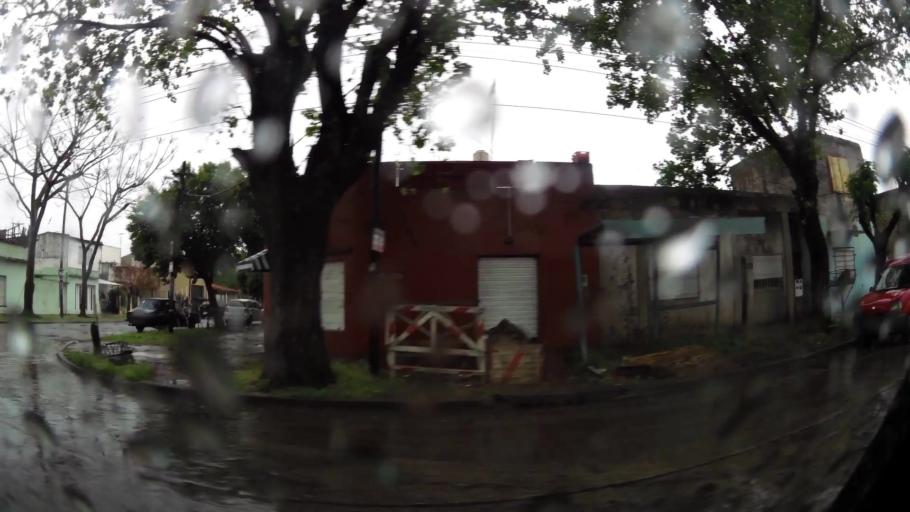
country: AR
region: Buenos Aires
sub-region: Partido de Lanus
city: Lanus
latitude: -34.7127
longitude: -58.4169
